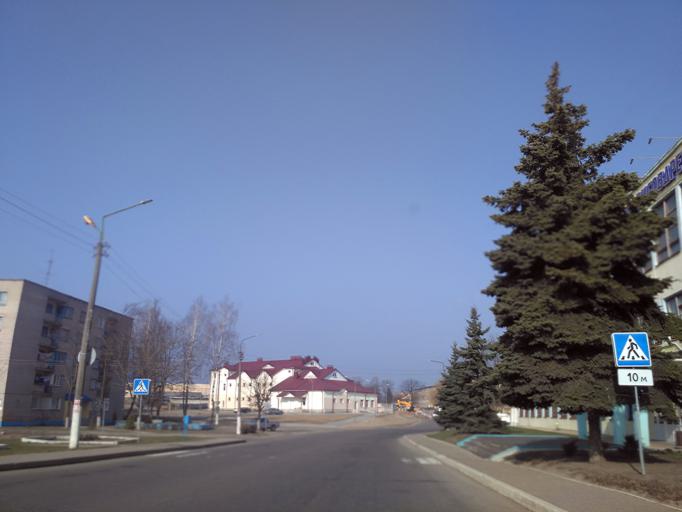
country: BY
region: Minsk
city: Horad Barysaw
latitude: 54.2270
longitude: 28.5227
